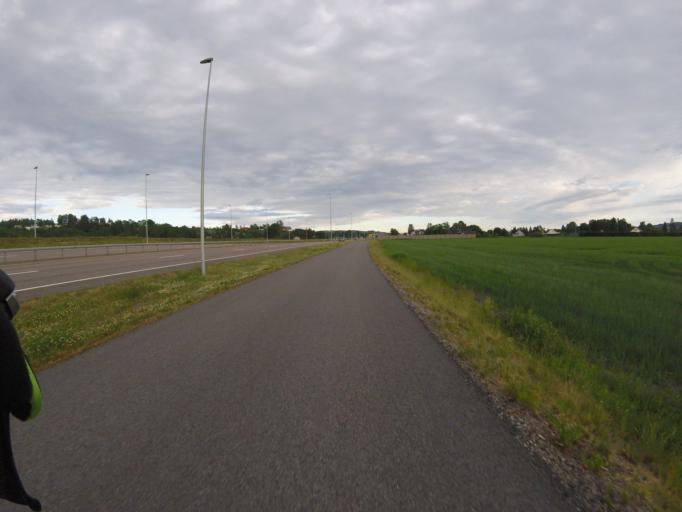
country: NO
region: Akershus
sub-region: Raelingen
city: Fjerdingby
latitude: 59.9490
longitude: 11.1046
